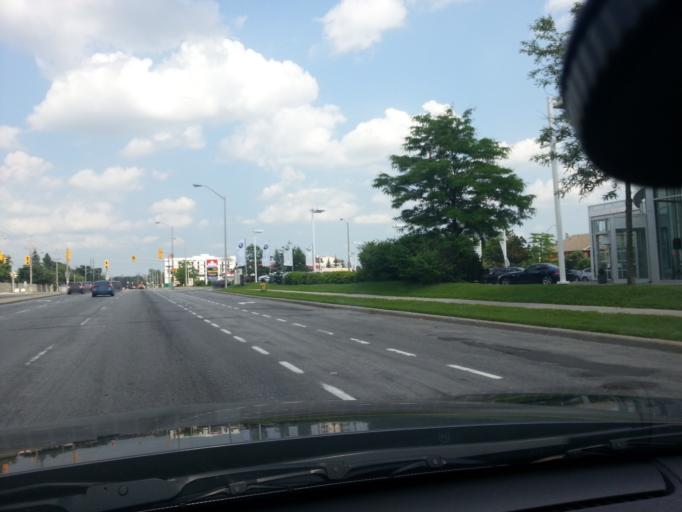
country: CA
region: Ontario
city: Ottawa
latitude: 45.3424
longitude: -75.6721
